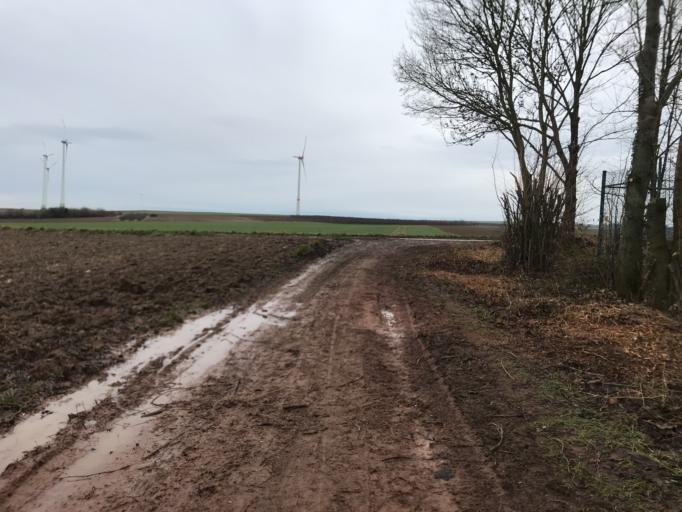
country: DE
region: Rheinland-Pfalz
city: Klein-Winternheim
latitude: 49.9433
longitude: 8.2245
